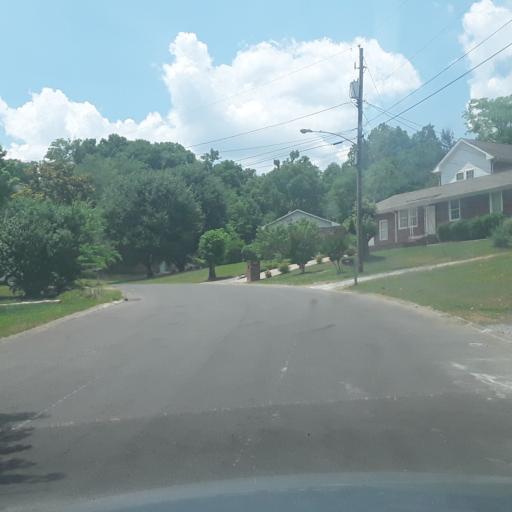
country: US
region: Tennessee
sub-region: Williamson County
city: Brentwood Estates
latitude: 36.0495
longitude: -86.6960
